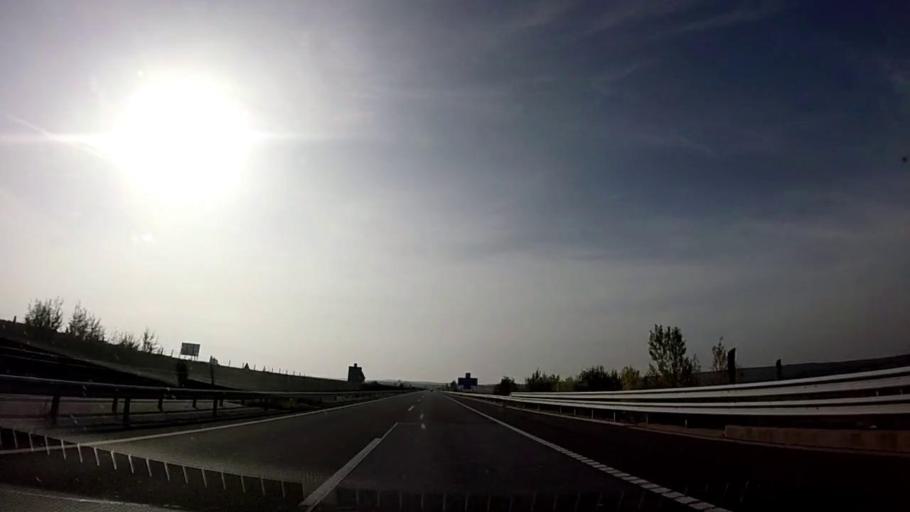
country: HU
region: Somogy
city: Zamardi
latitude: 46.8712
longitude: 17.9673
